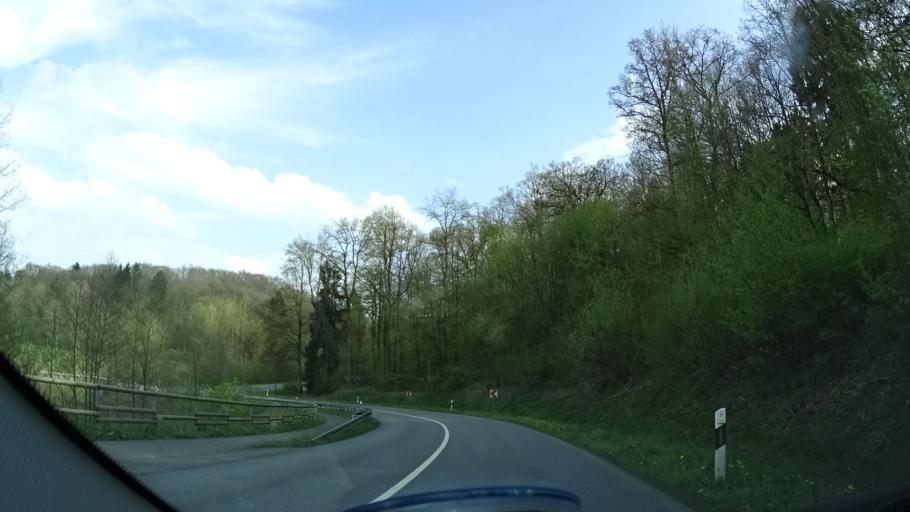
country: DE
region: North Rhine-Westphalia
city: Warstein
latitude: 51.4649
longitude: 8.3904
